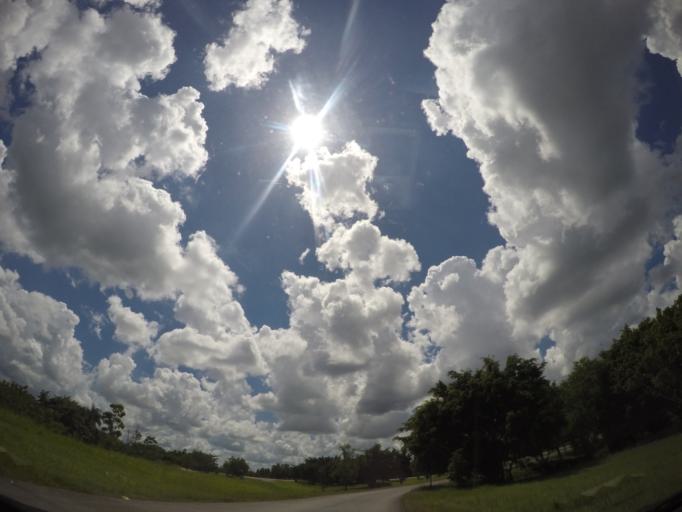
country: CU
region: La Habana
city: Havana
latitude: 23.1261
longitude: -82.4010
